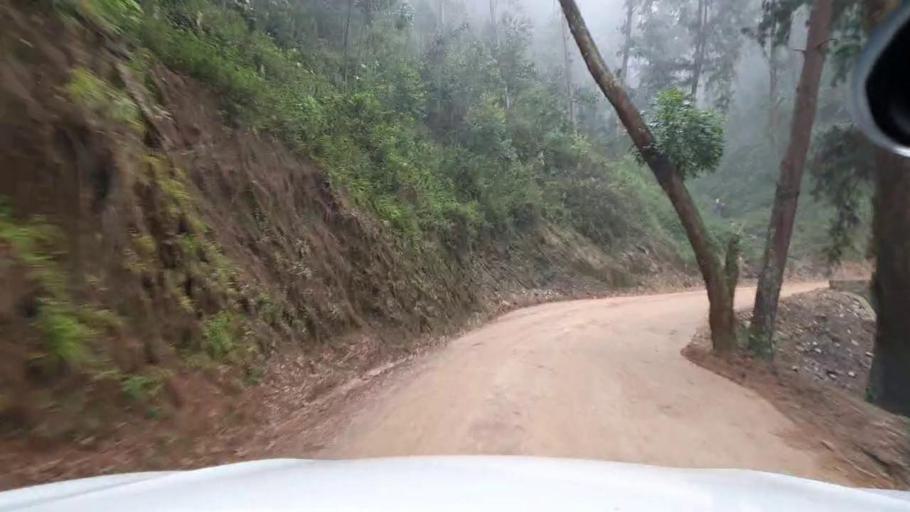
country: BI
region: Cibitoke
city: Cibitoke
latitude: -2.5935
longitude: 29.1932
